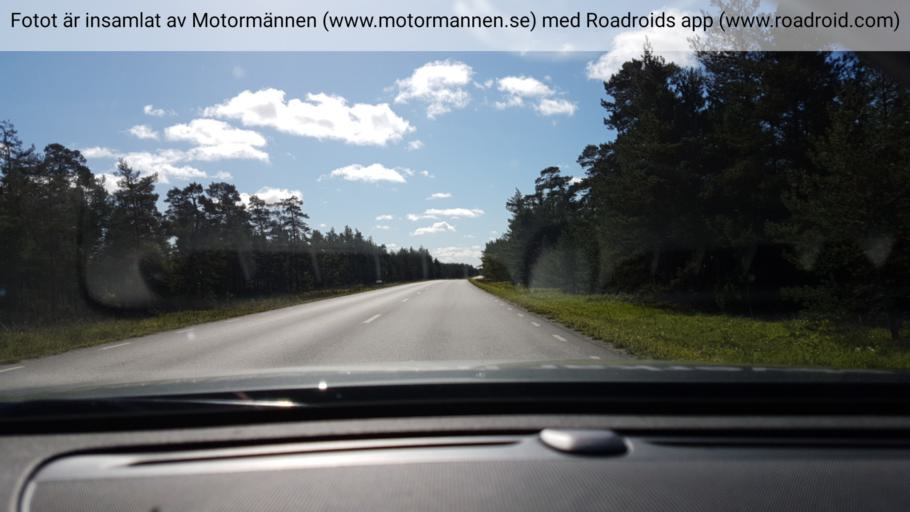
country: SE
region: Gotland
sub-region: Gotland
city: Slite
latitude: 57.7336
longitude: 18.7907
